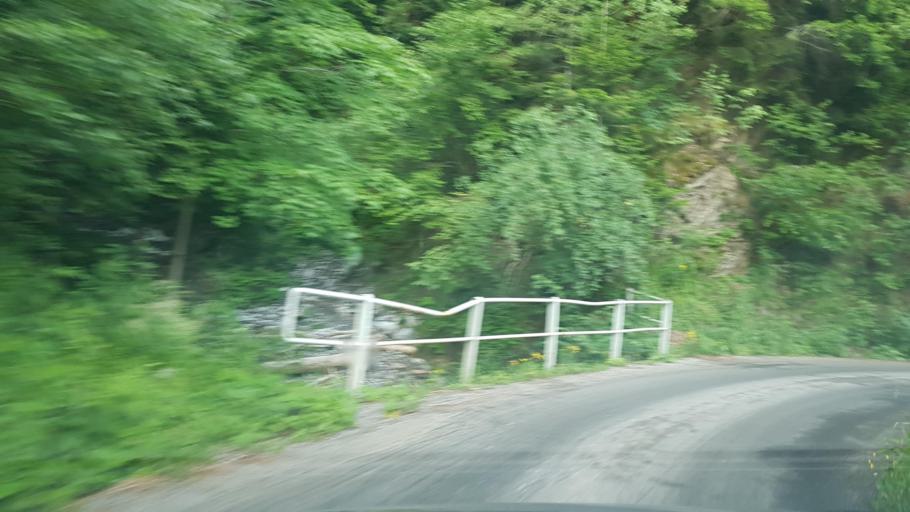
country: IT
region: Friuli Venezia Giulia
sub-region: Provincia di Udine
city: Paularo
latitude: 46.5599
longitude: 13.1247
